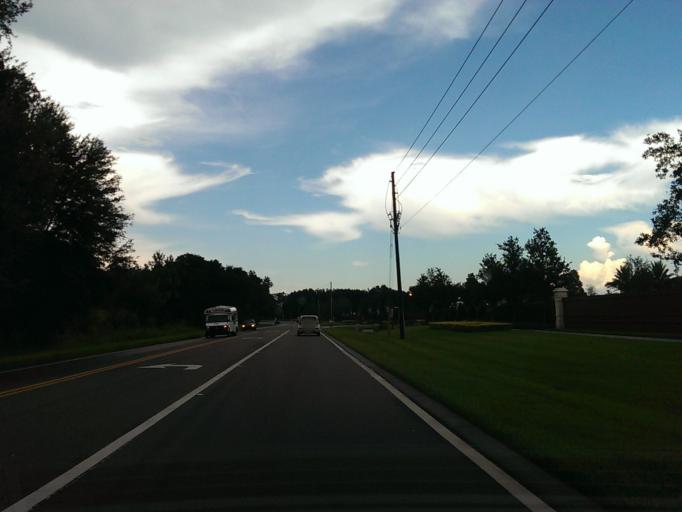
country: US
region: Florida
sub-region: Orange County
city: Bay Hill
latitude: 28.4331
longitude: -81.5617
